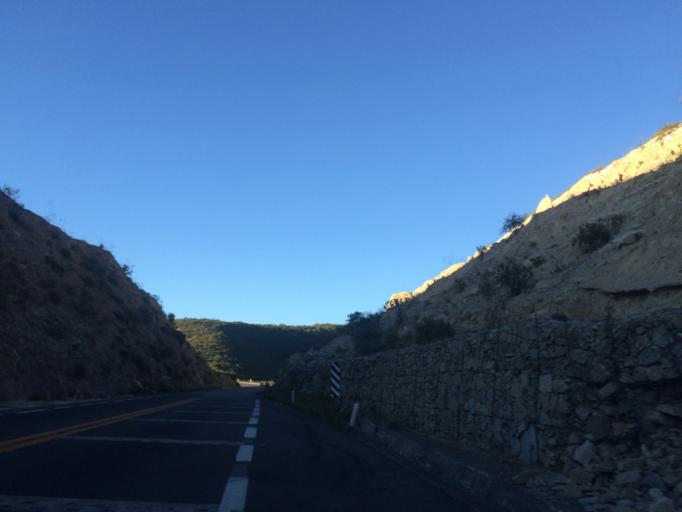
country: MX
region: Puebla
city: Chapuco
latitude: 18.6624
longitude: -97.4566
